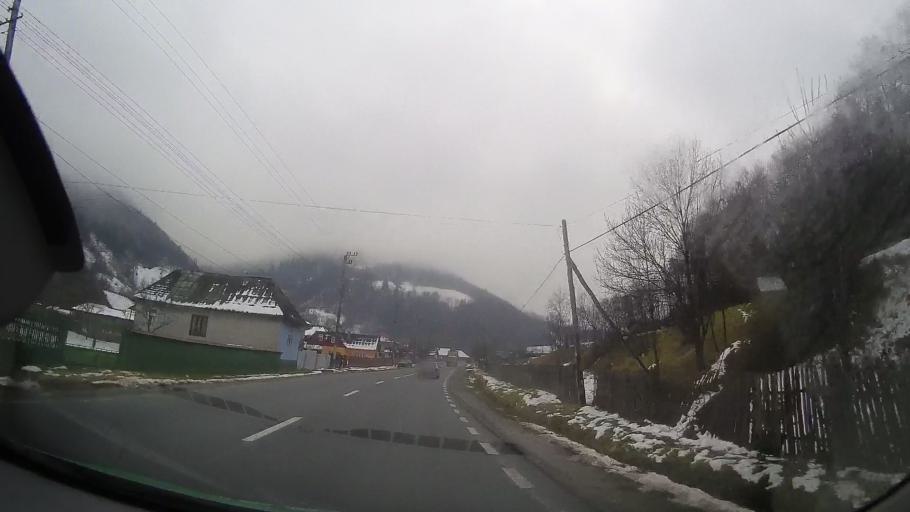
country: RO
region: Neamt
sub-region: Comuna Bicazu Ardelean
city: Bicazu Ardelean
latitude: 46.8557
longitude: 25.9358
